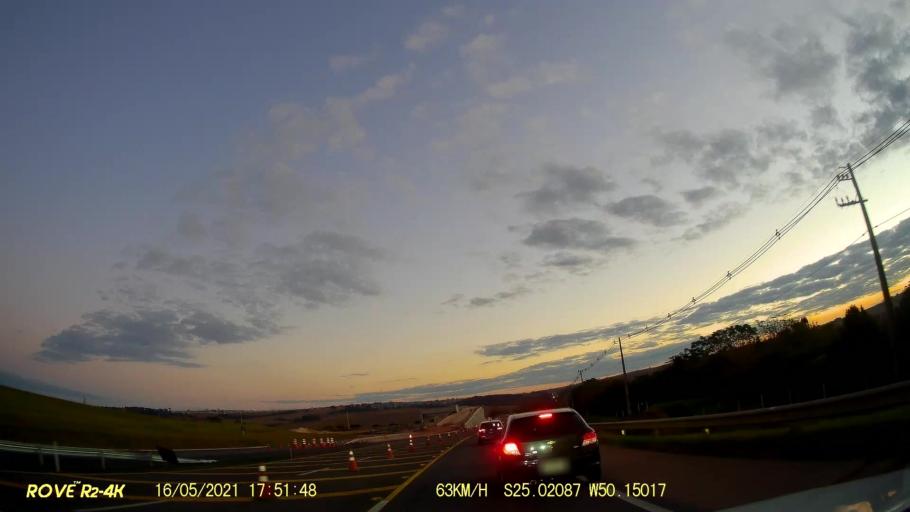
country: BR
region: Parana
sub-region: Ponta Grossa
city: Ponta Grossa
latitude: -25.0207
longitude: -50.1502
